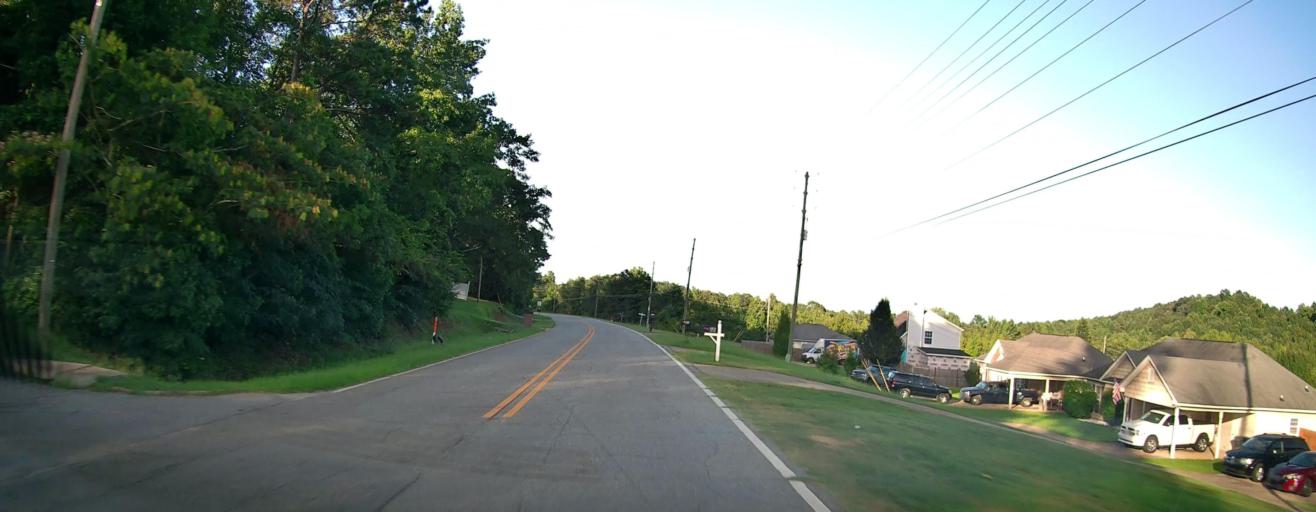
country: US
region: Georgia
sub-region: Muscogee County
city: Columbus
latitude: 32.4251
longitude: -85.0177
